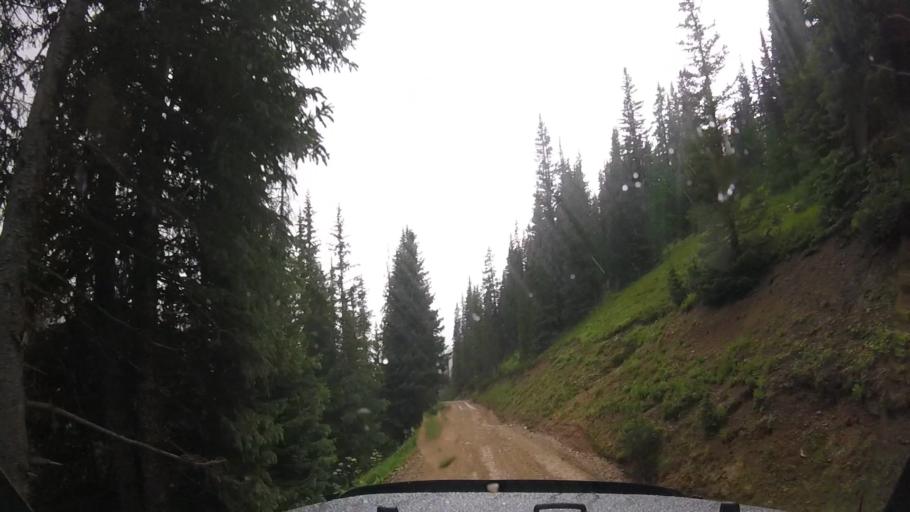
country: US
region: Colorado
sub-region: San Juan County
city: Silverton
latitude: 37.9066
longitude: -107.6461
